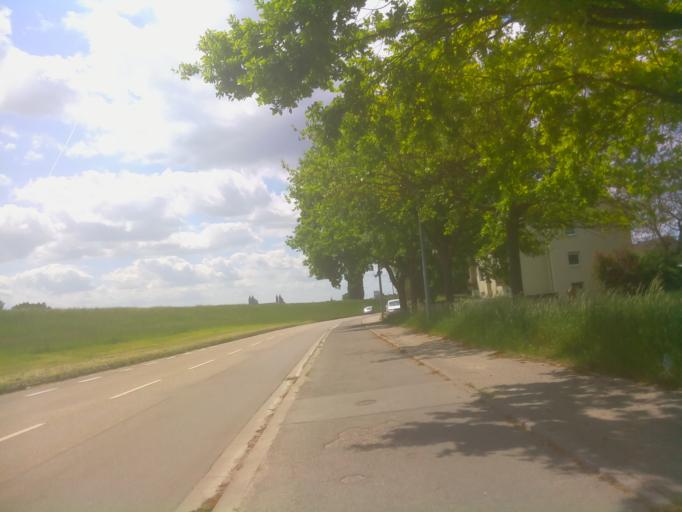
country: DE
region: Rheinland-Pfalz
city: Speyer
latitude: 49.3344
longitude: 8.4554
